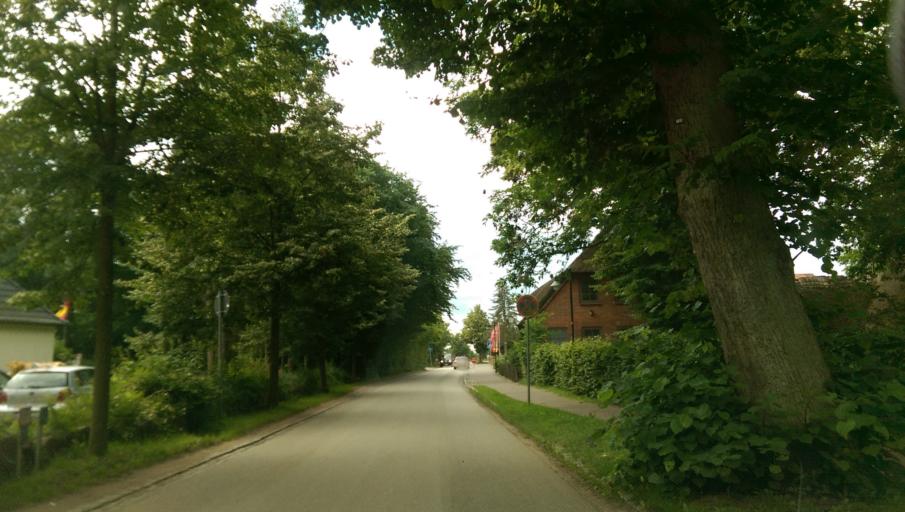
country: DE
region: Schleswig-Holstein
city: Travemuende
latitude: 53.9667
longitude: 10.8209
